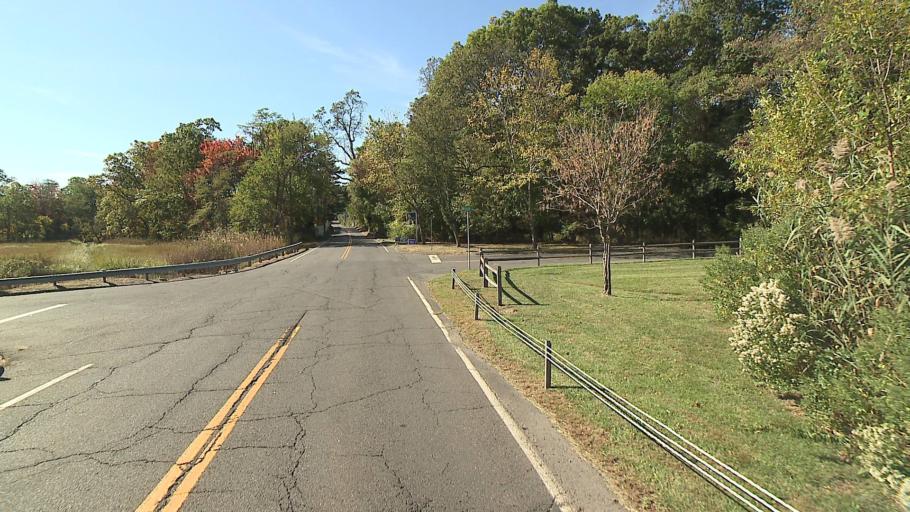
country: US
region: Connecticut
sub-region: Fairfield County
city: Darien
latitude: 41.0722
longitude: -73.4289
